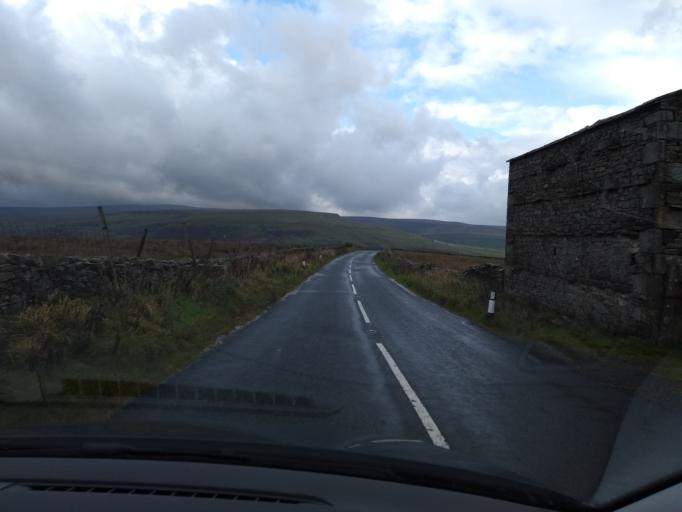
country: GB
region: England
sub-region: Cumbria
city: Kirkby Stephen
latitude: 54.3728
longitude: -2.1826
